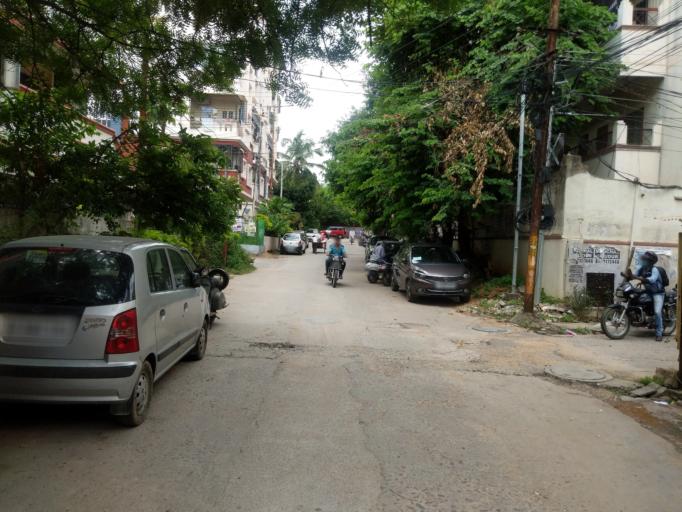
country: IN
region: Telangana
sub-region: Rangareddi
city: Kukatpalli
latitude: 17.4428
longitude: 78.4359
